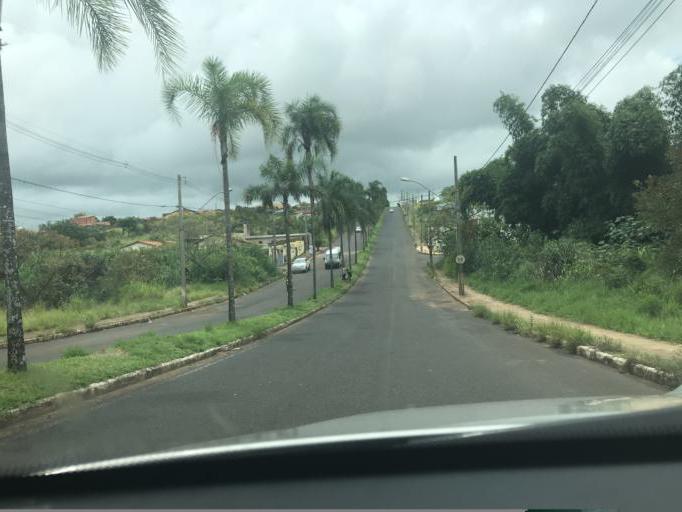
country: BR
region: Minas Gerais
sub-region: Araxa
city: Araxa
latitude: -19.5779
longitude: -46.9323
